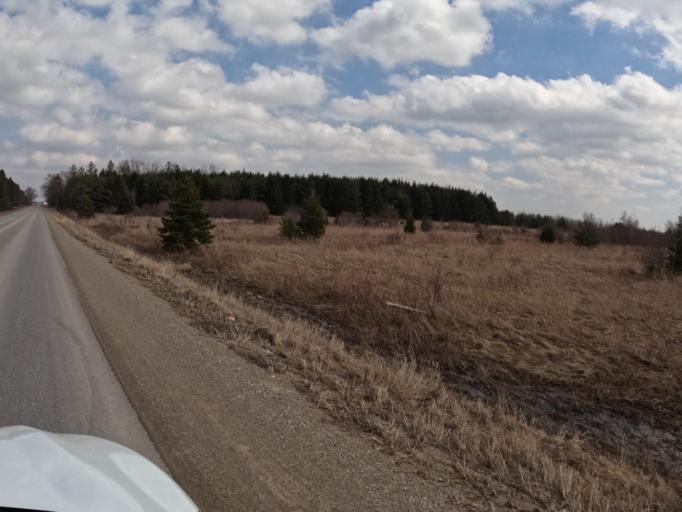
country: CA
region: Ontario
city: Shelburne
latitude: 44.0018
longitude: -80.2419
